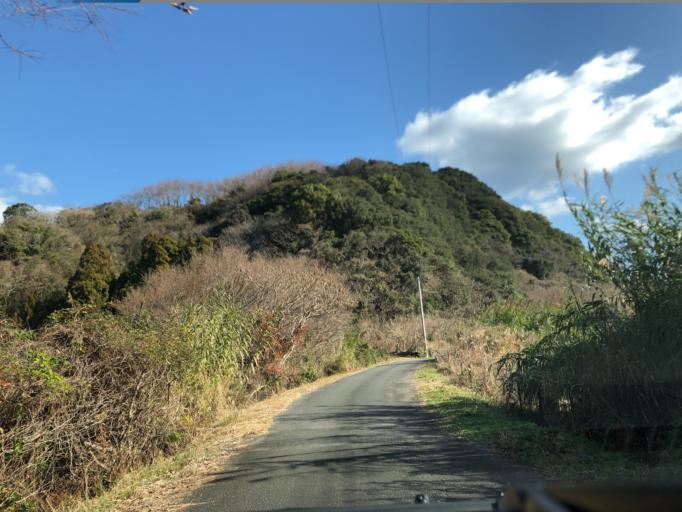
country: JP
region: Kochi
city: Sukumo
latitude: 32.9118
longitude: 132.6974
